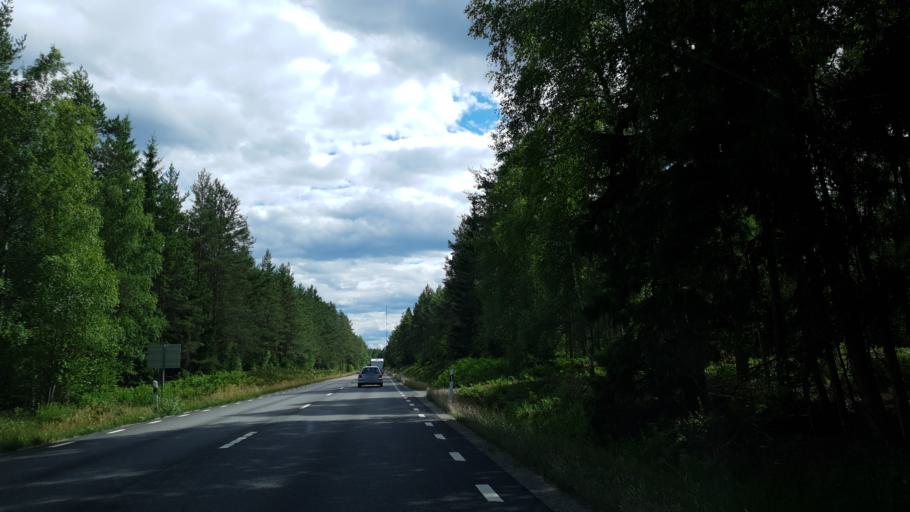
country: SE
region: Kronoberg
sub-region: Lessebo Kommun
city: Lessebo
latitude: 56.7860
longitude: 15.4144
